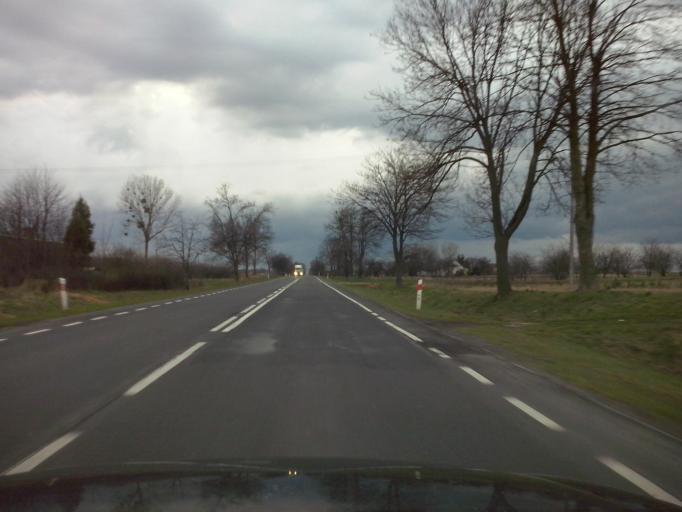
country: PL
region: Lublin Voivodeship
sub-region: Powiat chelmski
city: Rejowiec Fabryczny
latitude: 51.1714
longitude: 23.3040
